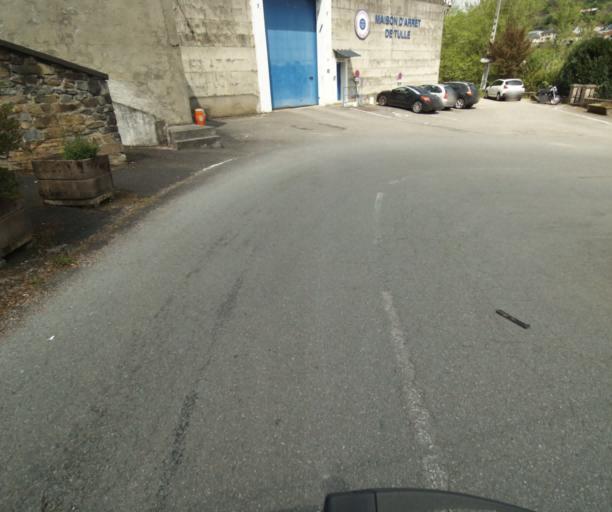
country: FR
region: Limousin
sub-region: Departement de la Correze
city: Tulle
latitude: 45.2749
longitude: 1.7693
